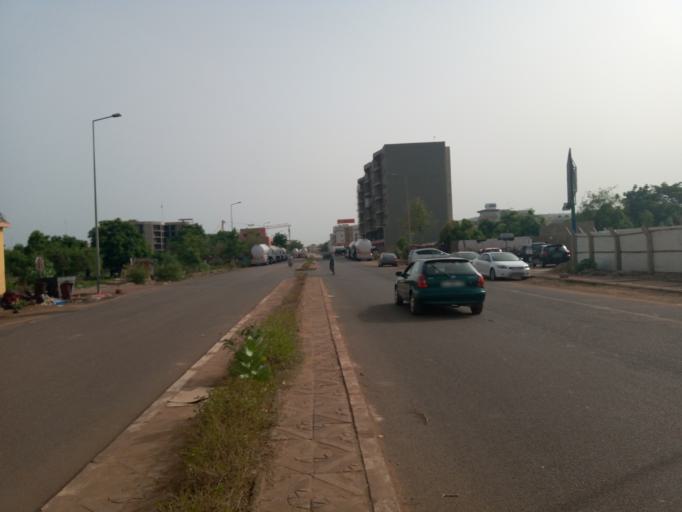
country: ML
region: Bamako
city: Bamako
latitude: 12.6296
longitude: -8.0279
